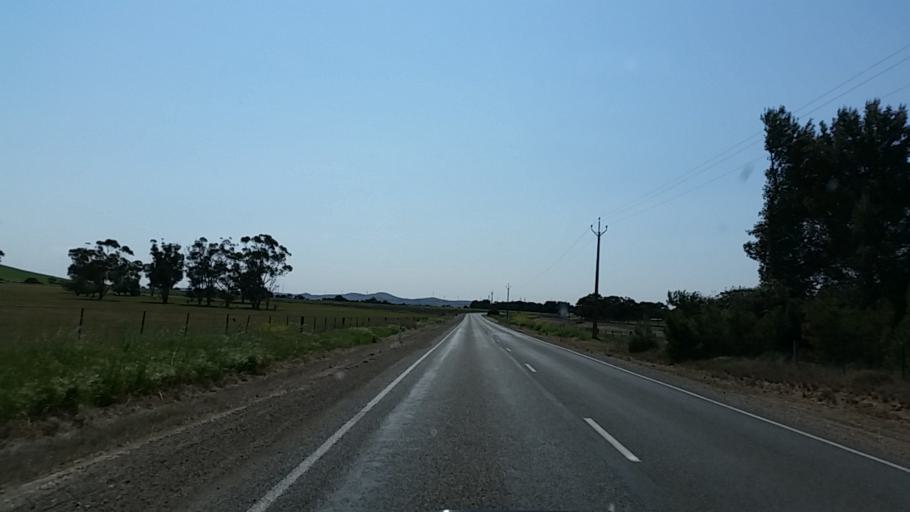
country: AU
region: South Australia
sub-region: Northern Areas
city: Jamestown
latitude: -33.1857
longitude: 138.4677
